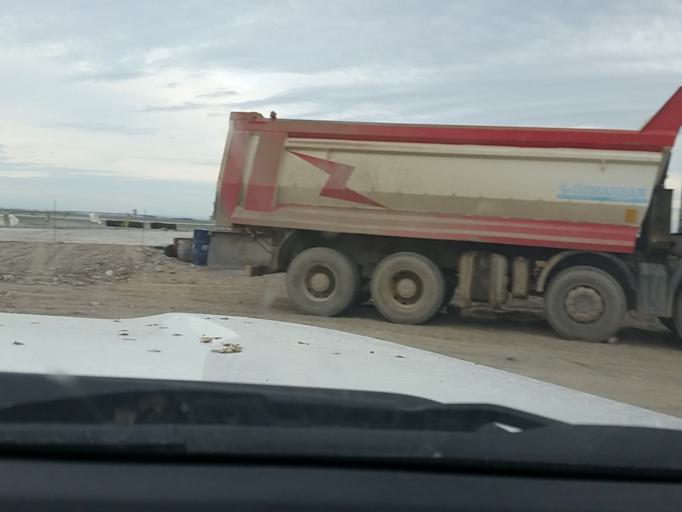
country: KZ
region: Almaty Oblysy
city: Zharkent
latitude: 44.1720
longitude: 80.3467
